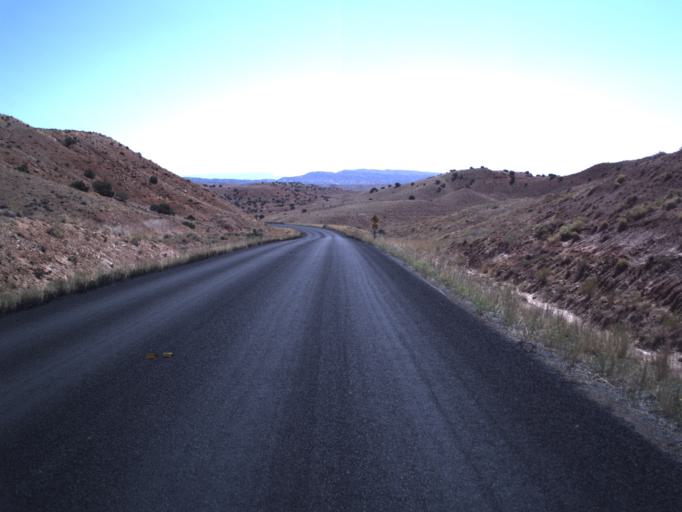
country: US
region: Utah
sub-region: Uintah County
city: Maeser
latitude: 40.4095
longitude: -109.7059
